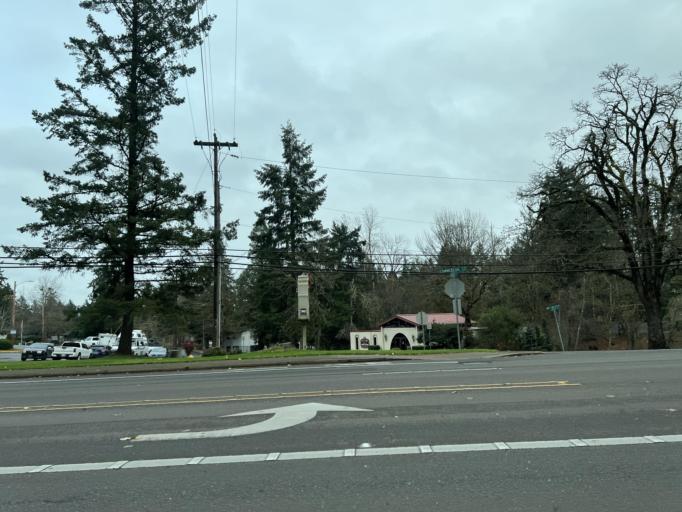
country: US
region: Oregon
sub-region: Marion County
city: Salem
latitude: 44.8962
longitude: -123.0373
